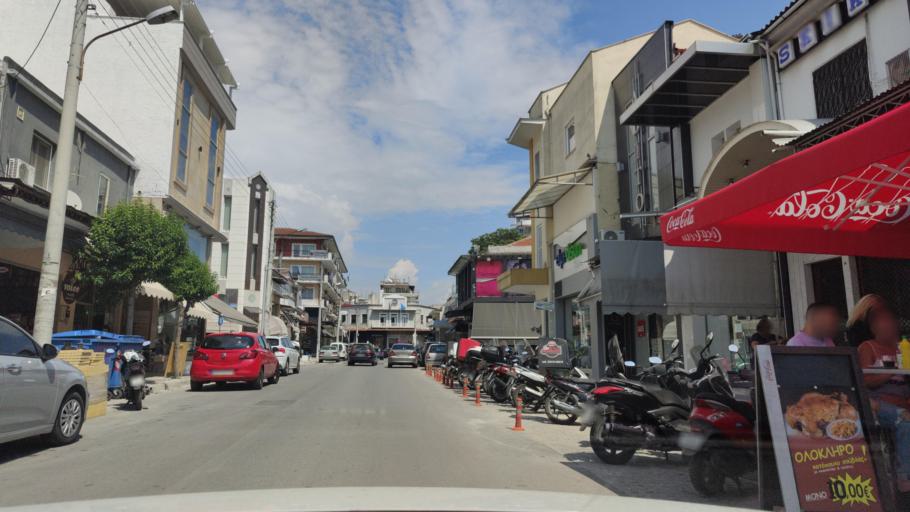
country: GR
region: Central Macedonia
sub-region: Nomos Serron
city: Serres
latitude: 41.0899
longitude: 23.5483
